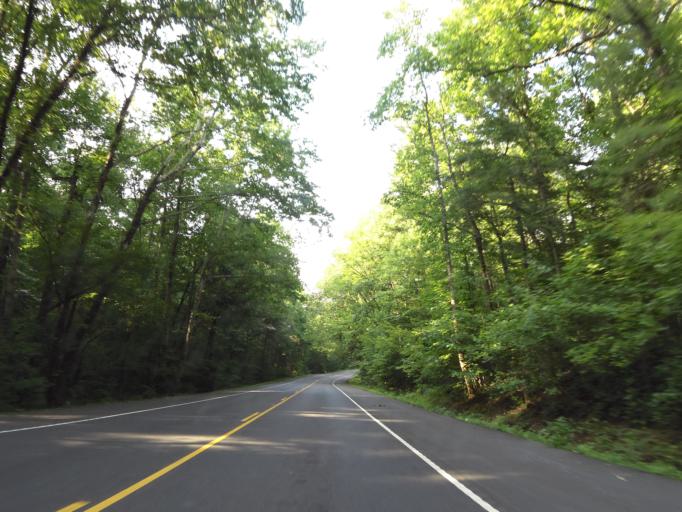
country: US
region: Tennessee
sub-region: Anderson County
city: Oak Ridge
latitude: 35.9054
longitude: -84.3309
